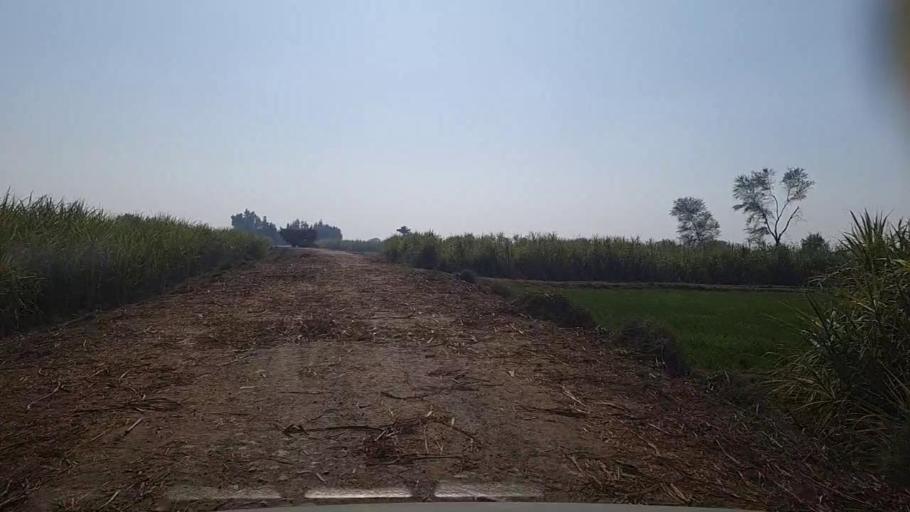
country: PK
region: Sindh
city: Mirpur Mathelo
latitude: 28.0691
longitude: 69.6172
